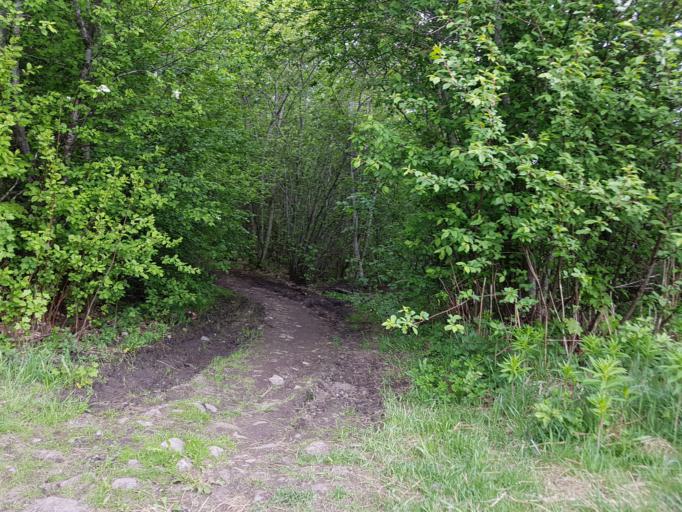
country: NO
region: Nord-Trondelag
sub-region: Levanger
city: Levanger
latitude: 63.7389
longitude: 11.2592
